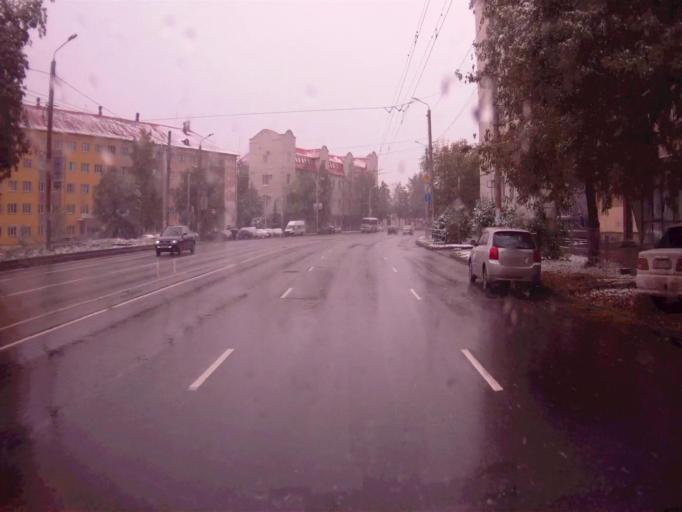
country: RU
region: Chelyabinsk
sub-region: Gorod Chelyabinsk
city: Chelyabinsk
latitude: 55.1475
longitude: 61.4164
